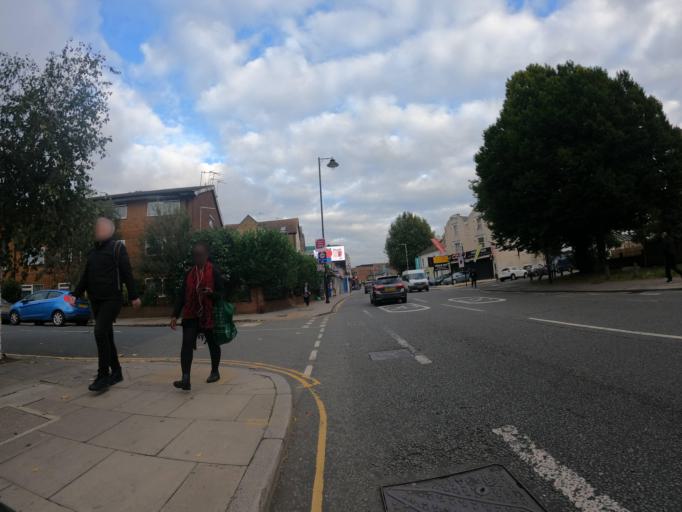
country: GB
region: England
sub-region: Greater London
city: Ealing
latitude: 51.5097
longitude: -0.3294
